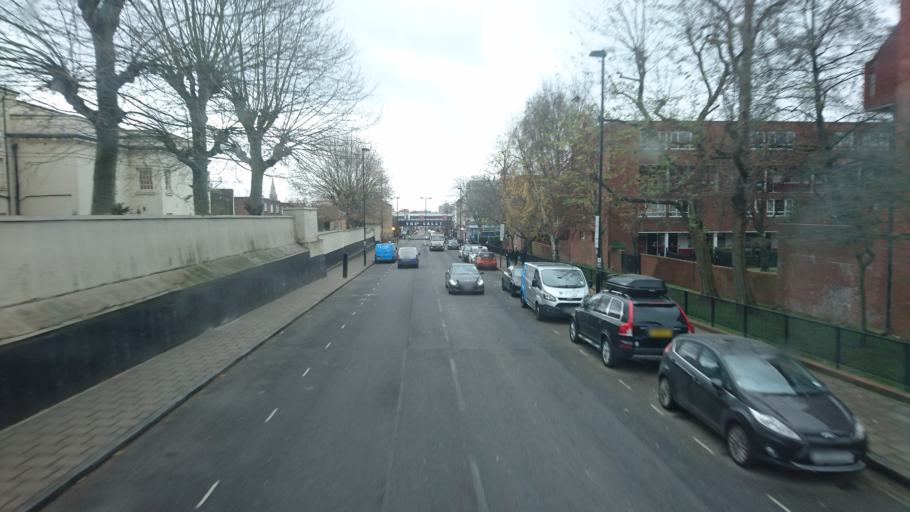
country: GB
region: England
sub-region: Greater London
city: Barnsbury
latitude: 51.5448
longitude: -0.1177
